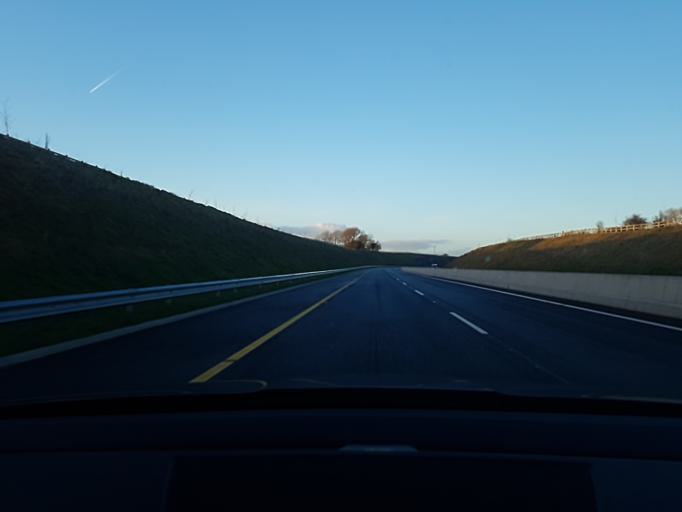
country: IE
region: Connaught
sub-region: County Galway
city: Tuam
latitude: 53.4434
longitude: -8.8492
